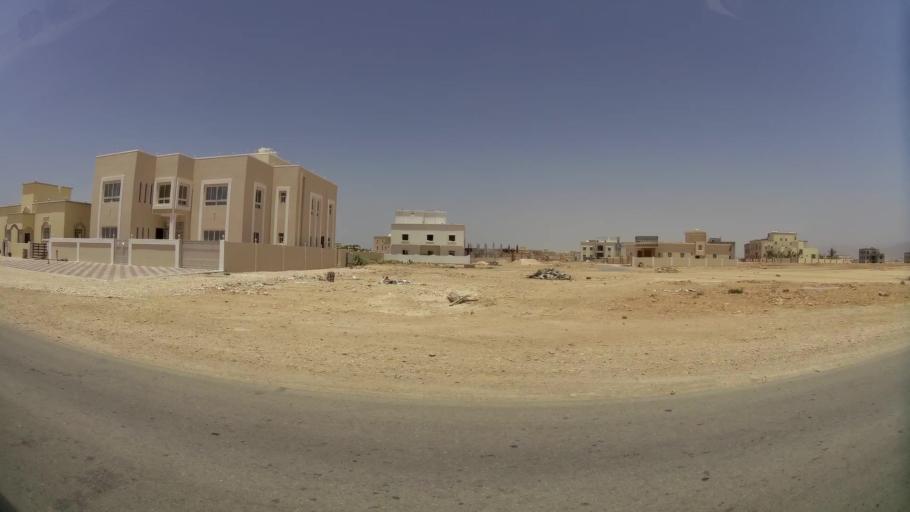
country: OM
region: Zufar
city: Salalah
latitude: 17.0963
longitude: 54.1711
